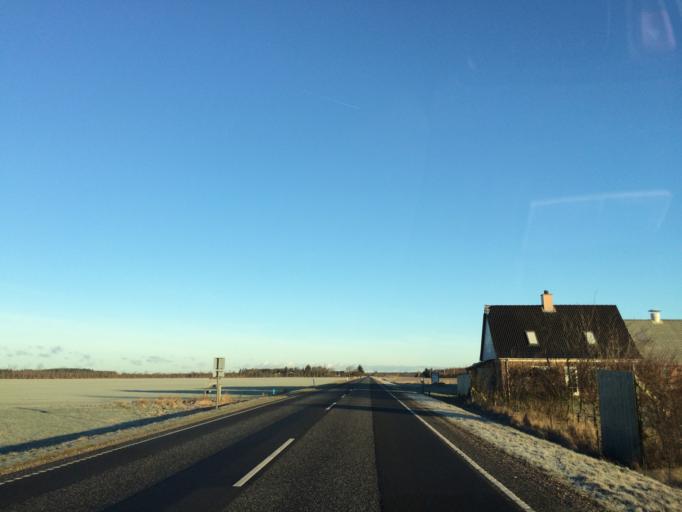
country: DK
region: Central Jutland
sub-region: Lemvig Kommune
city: Lemvig
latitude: 56.4386
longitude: 8.2968
